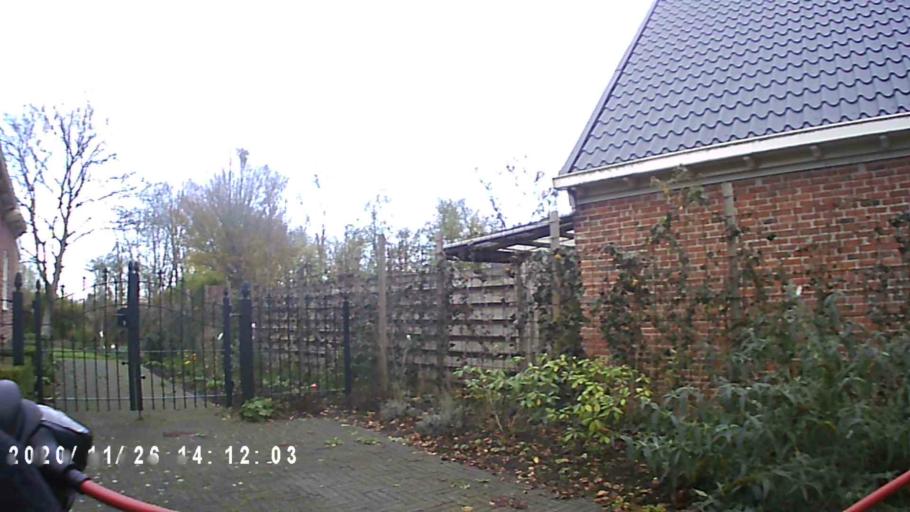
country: NL
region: Groningen
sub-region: Gemeente Delfzijl
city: Delfzijl
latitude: 53.3330
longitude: 6.8963
